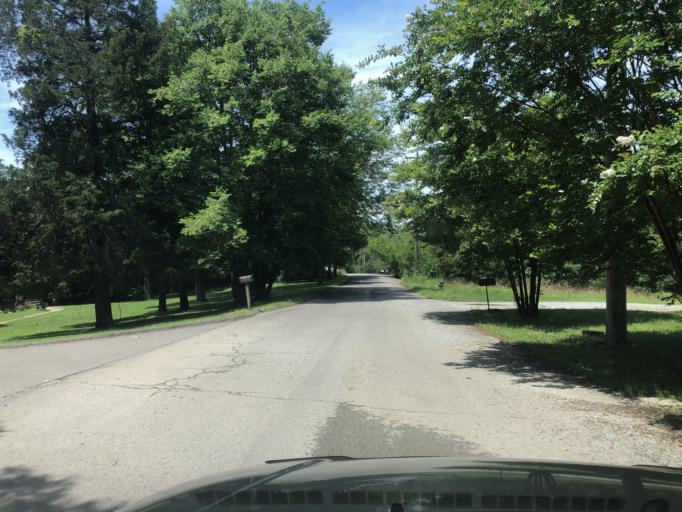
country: US
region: Tennessee
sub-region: Davidson County
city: Lakewood
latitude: 36.2503
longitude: -86.6811
